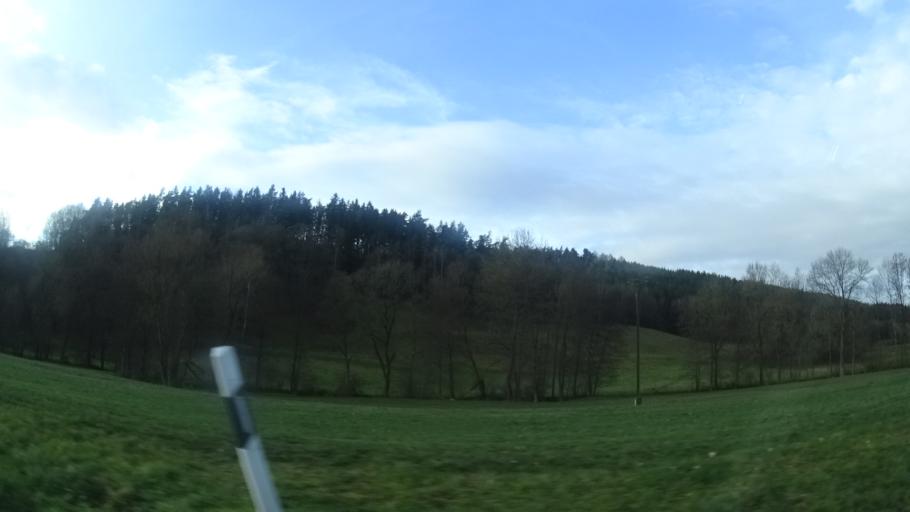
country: DE
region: Thuringia
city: Rottenbach
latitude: 50.6996
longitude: 11.2064
